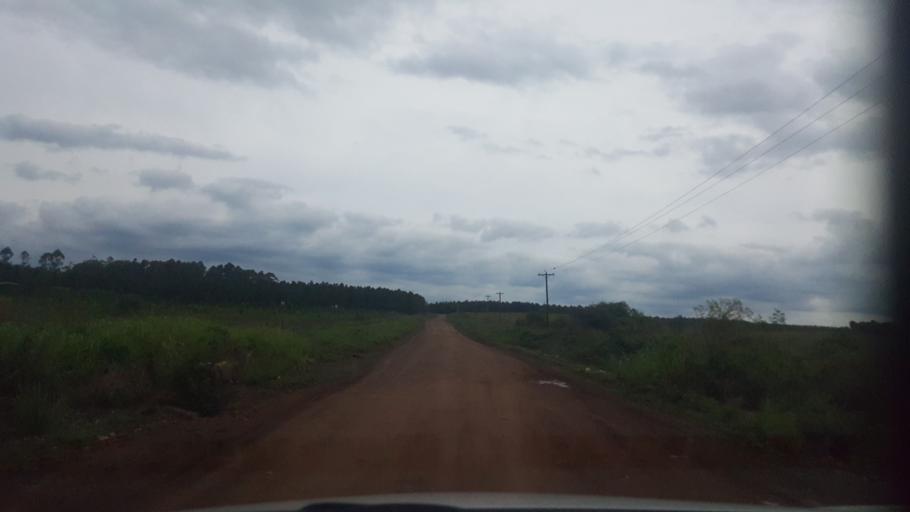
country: AR
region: Misiones
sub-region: Departamento de Candelaria
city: Candelaria
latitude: -27.5044
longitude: -55.7367
